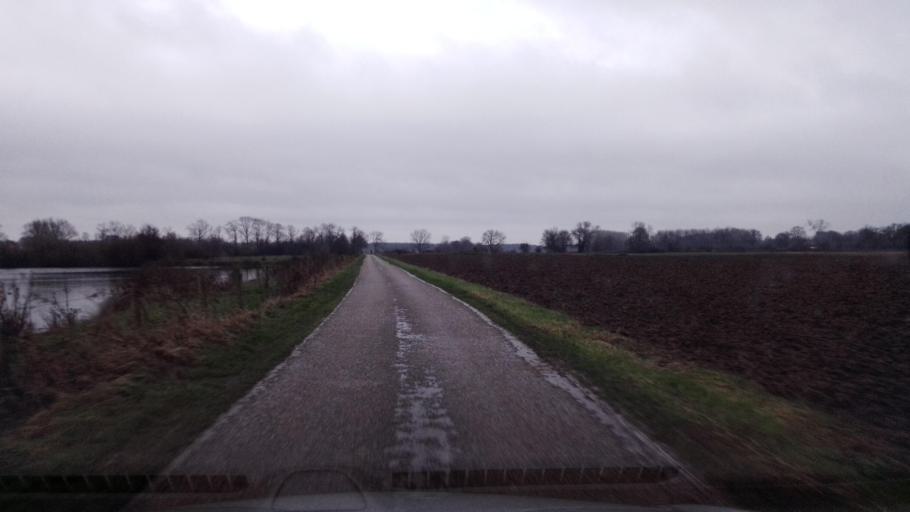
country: NL
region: Limburg
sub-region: Gemeente Venlo
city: Arcen
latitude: 51.4794
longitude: 6.1692
